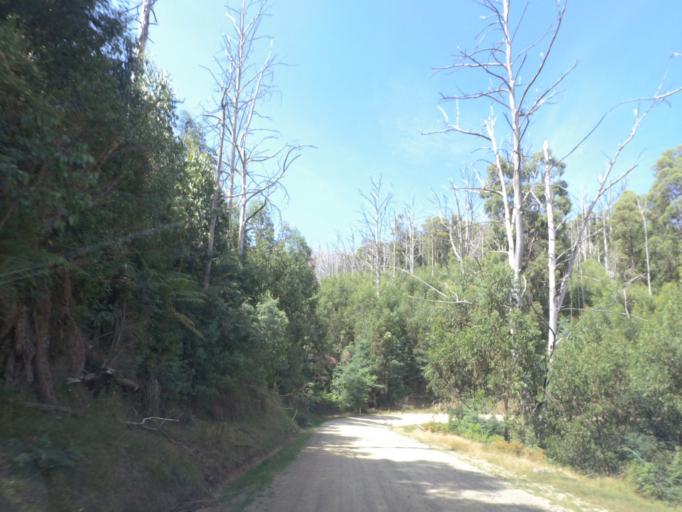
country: AU
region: Victoria
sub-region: Murrindindi
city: Alexandra
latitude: -37.4624
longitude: 145.7867
